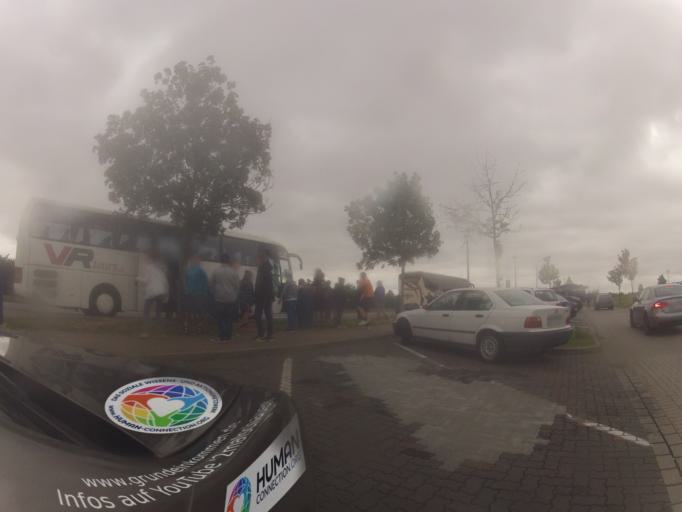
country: DE
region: Brandenburg
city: Schonfeld
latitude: 53.3950
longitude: 13.9928
